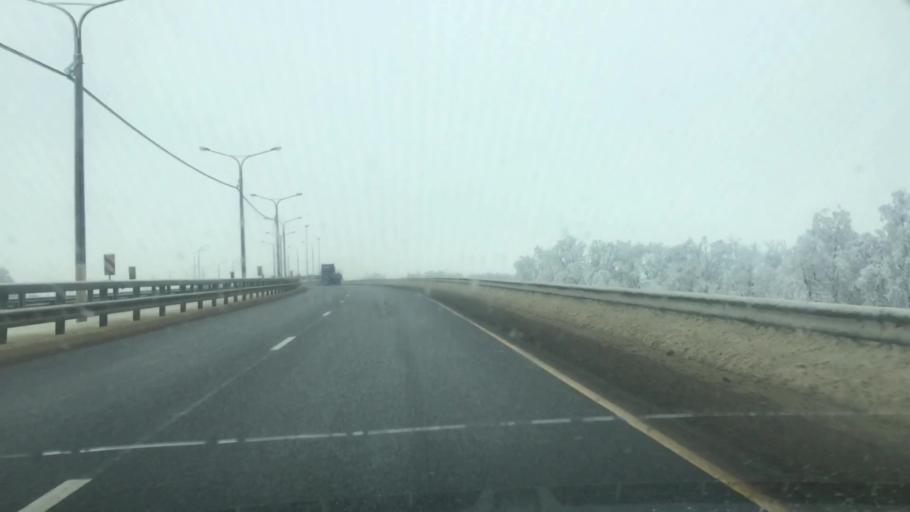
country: RU
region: Lipetsk
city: Yelets
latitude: 52.5469
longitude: 38.7189
